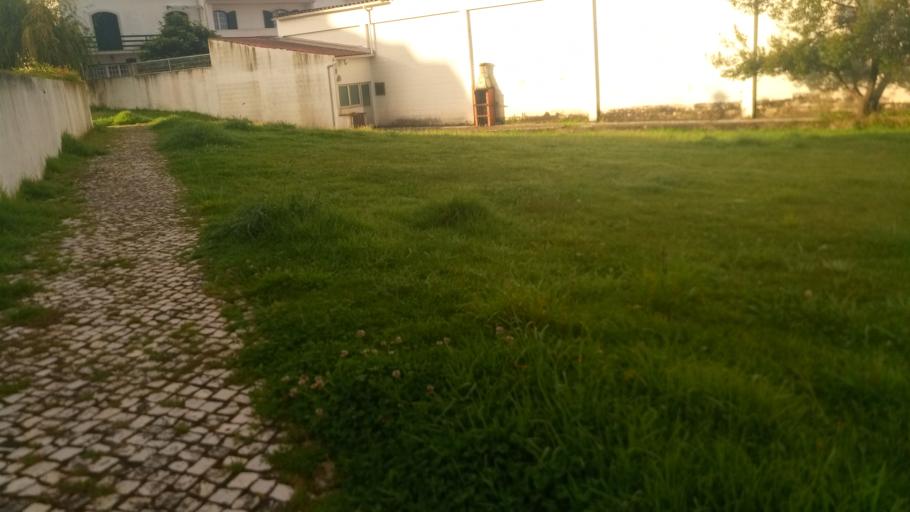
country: PT
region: Leiria
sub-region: Caldas da Rainha
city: Caldas da Rainha
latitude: 39.4149
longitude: -9.1392
